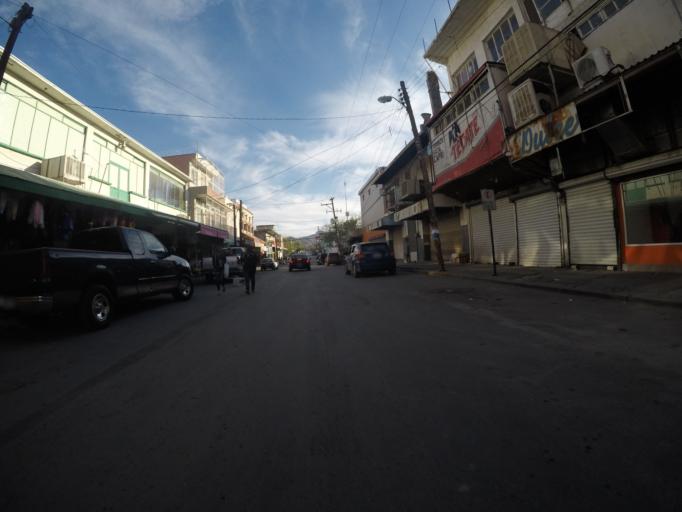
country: MX
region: Chihuahua
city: Ciudad Juarez
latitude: 31.7375
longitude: -106.4882
